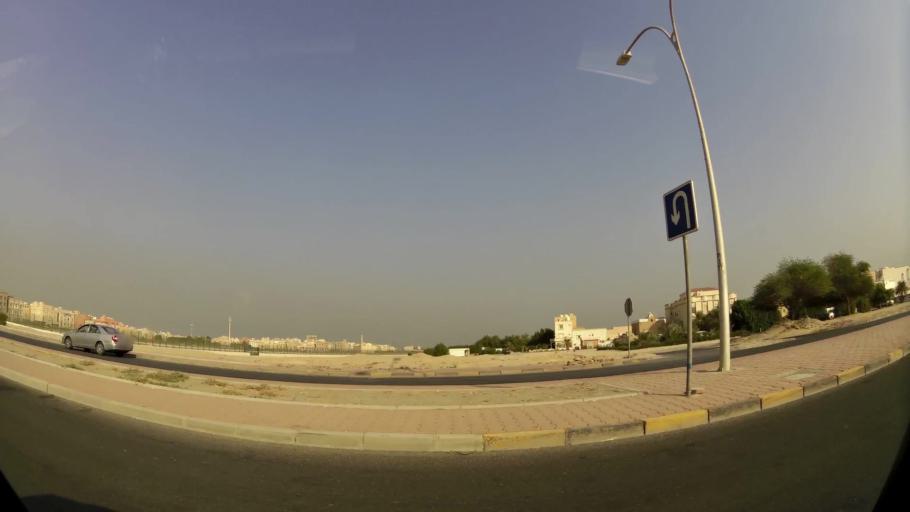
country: KW
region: Al Ahmadi
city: Ar Riqqah
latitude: 29.1191
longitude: 48.1050
